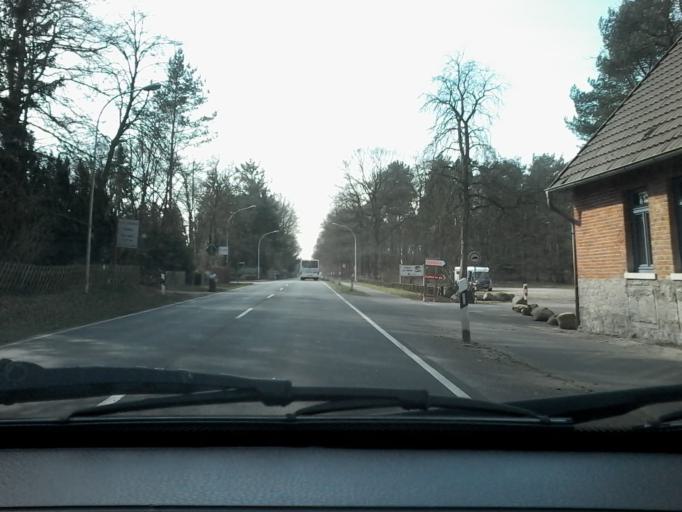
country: DE
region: Lower Saxony
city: Verden
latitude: 52.9308
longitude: 9.2717
